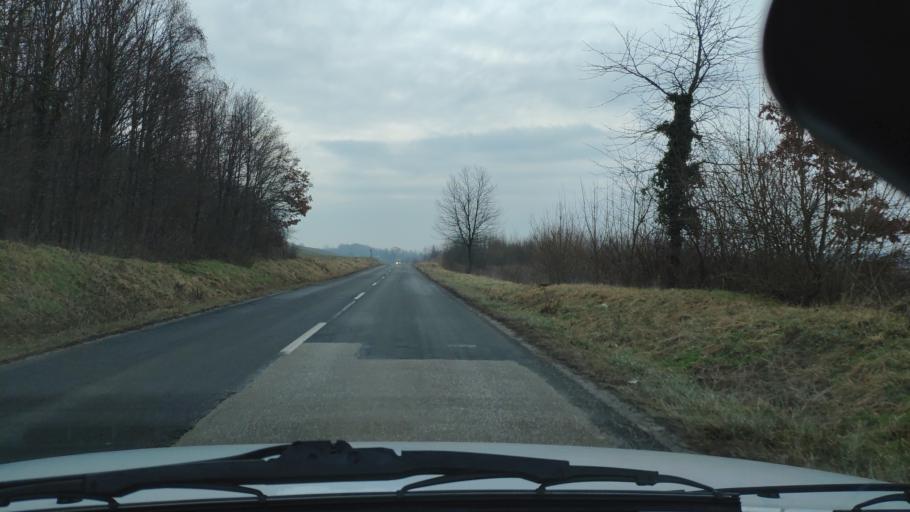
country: HU
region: Zala
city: Nagykanizsa
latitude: 46.5274
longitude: 16.9822
